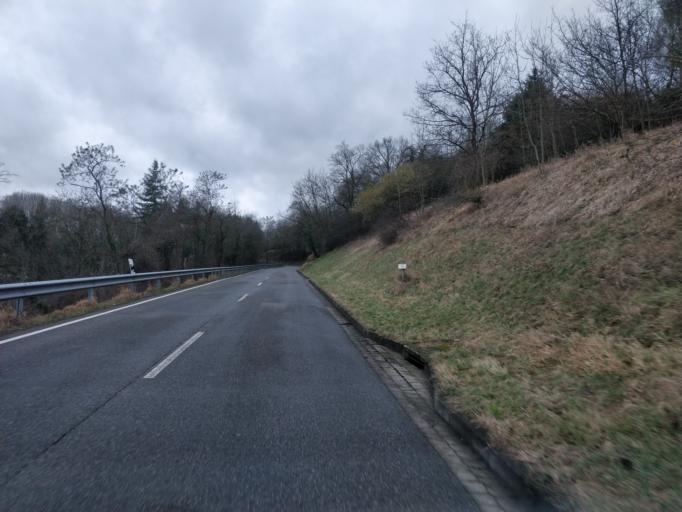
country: DE
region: Rheinland-Pfalz
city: Andernach
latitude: 50.4533
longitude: 7.4160
